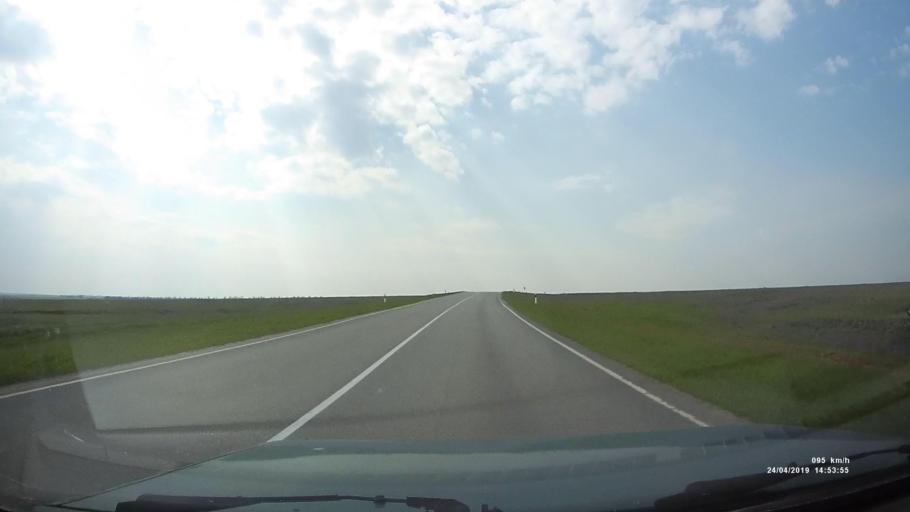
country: RU
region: Rostov
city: Remontnoye
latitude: 46.5320
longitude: 43.6486
